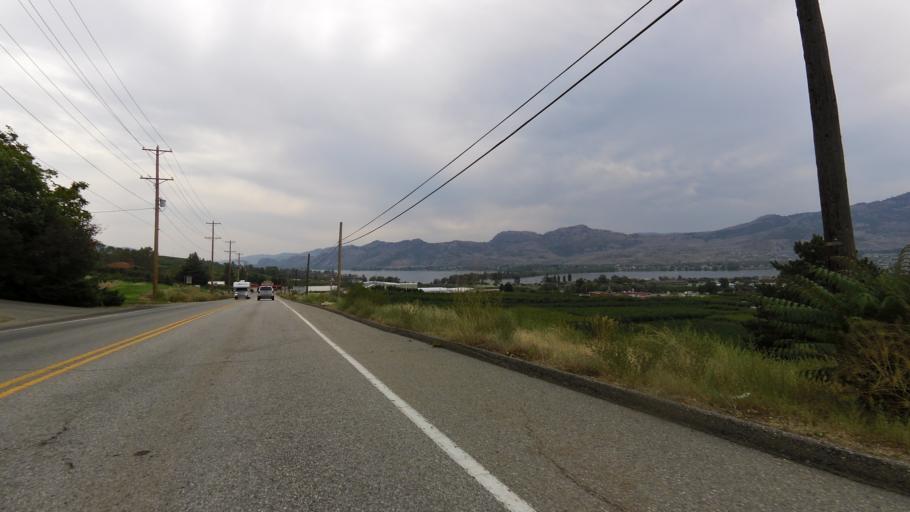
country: CA
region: British Columbia
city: Osoyoos
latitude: 49.0310
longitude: -119.4312
